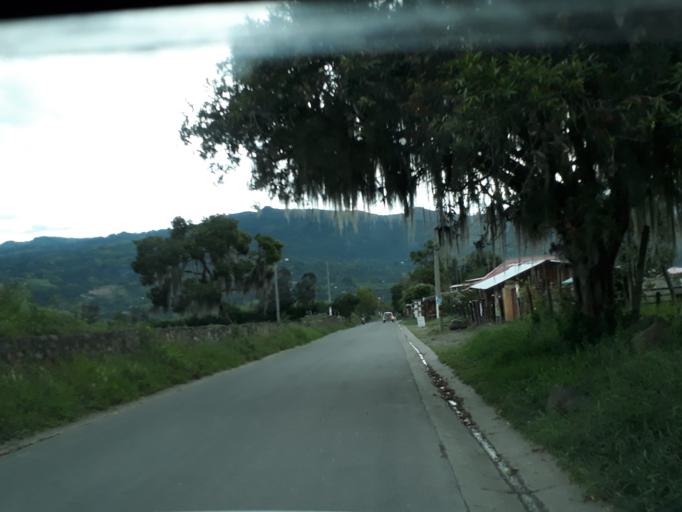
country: CO
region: Cundinamarca
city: Pacho
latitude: 5.1537
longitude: -74.1444
